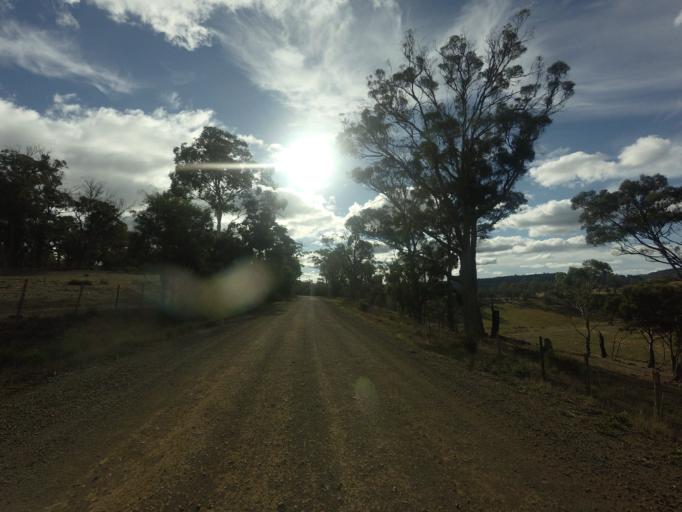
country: AU
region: Tasmania
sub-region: Brighton
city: Bridgewater
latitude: -42.4565
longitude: 147.2495
